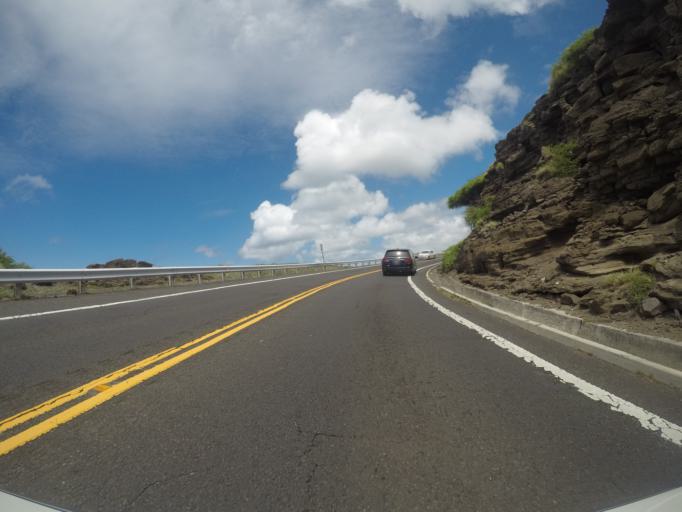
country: US
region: Hawaii
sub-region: Honolulu County
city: Waimanalo Beach
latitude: 21.2731
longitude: -157.6890
